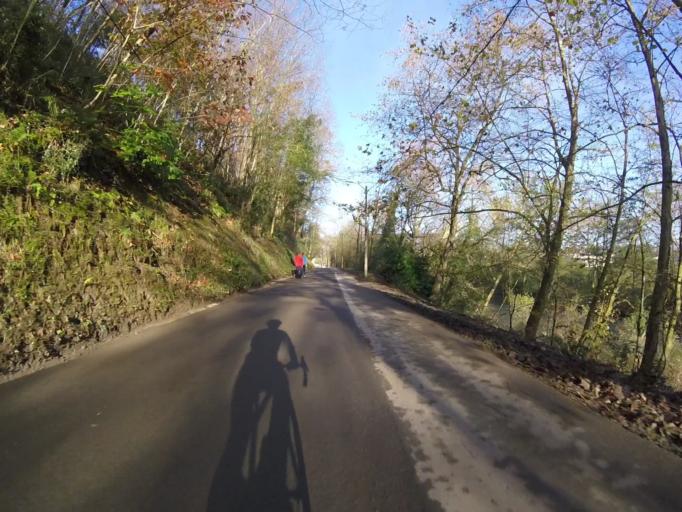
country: ES
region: Basque Country
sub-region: Provincia de Guipuzcoa
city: Usurbil
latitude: 43.2635
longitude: -2.0536
